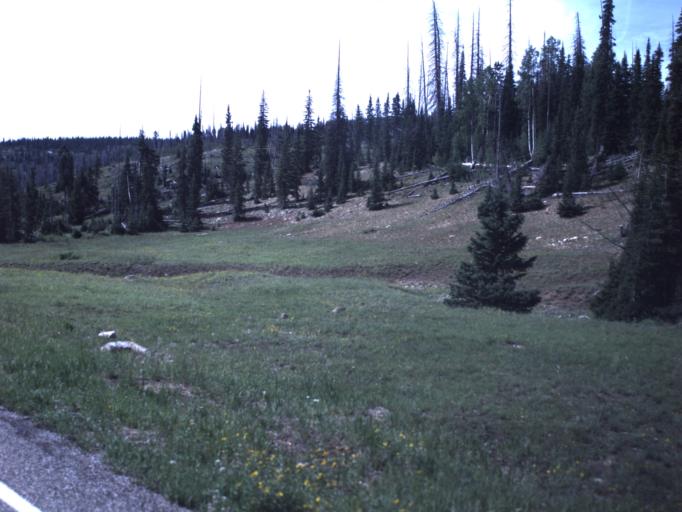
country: US
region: Utah
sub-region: Iron County
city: Cedar City
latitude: 37.5815
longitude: -112.8446
